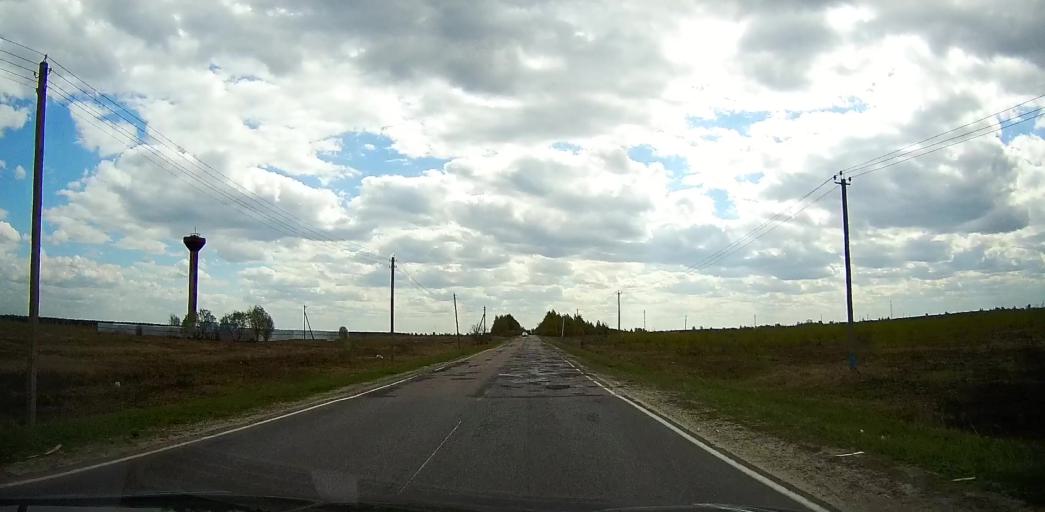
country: RU
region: Moskovskaya
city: Davydovo
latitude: 55.6401
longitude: 38.7487
